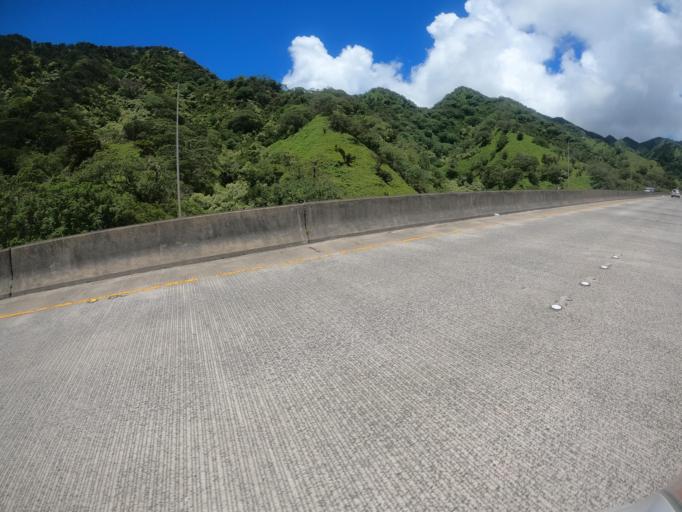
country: US
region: Hawaii
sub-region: Honolulu County
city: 'Ahuimanu
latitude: 21.4055
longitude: -157.8678
